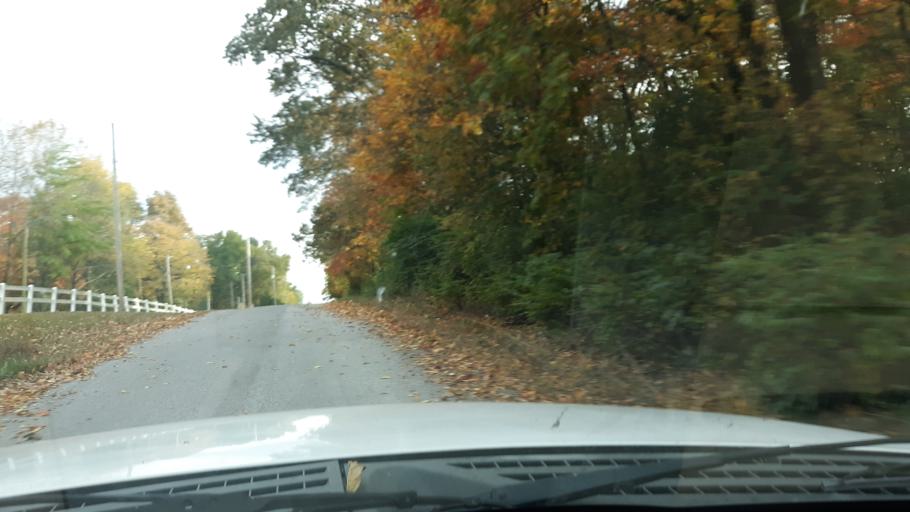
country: US
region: Illinois
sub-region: Saline County
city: Eldorado
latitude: 37.8291
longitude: -88.5025
